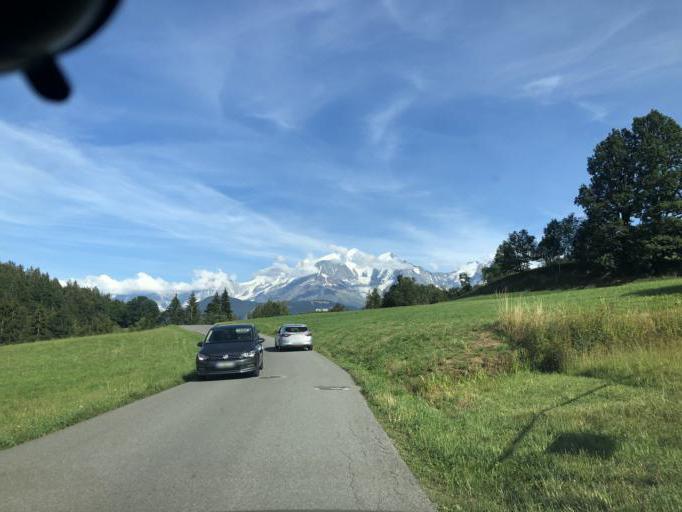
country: FR
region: Rhone-Alpes
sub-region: Departement de la Haute-Savoie
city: Cordon
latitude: 45.9137
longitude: 6.6164
